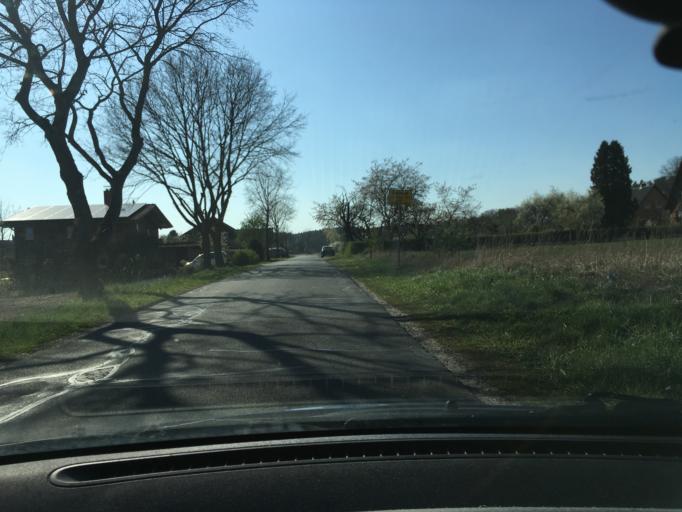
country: DE
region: Lower Saxony
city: Hitzacker
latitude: 53.1526
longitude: 11.0070
